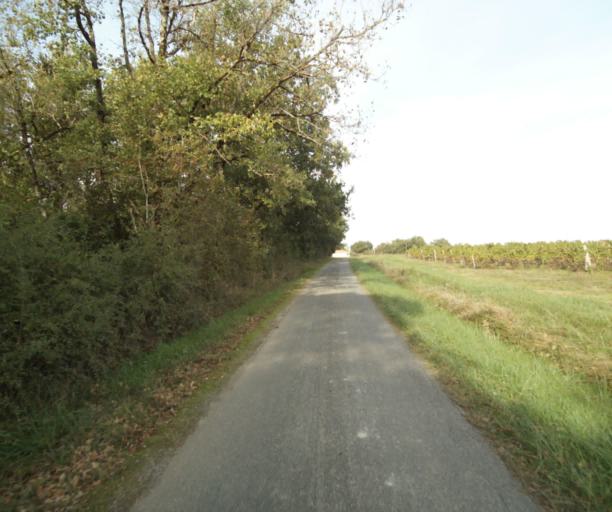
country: FR
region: Midi-Pyrenees
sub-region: Departement du Tarn-et-Garonne
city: Campsas
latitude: 43.9234
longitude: 1.3252
